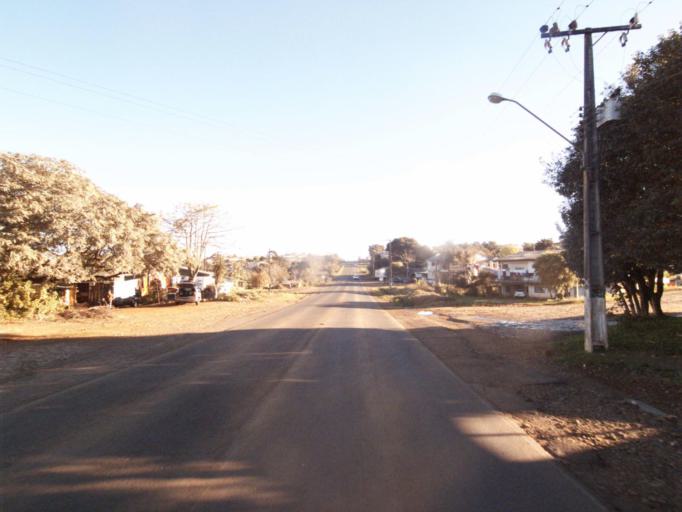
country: AR
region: Misiones
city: Bernardo de Irigoyen
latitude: -26.2616
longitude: -53.6208
